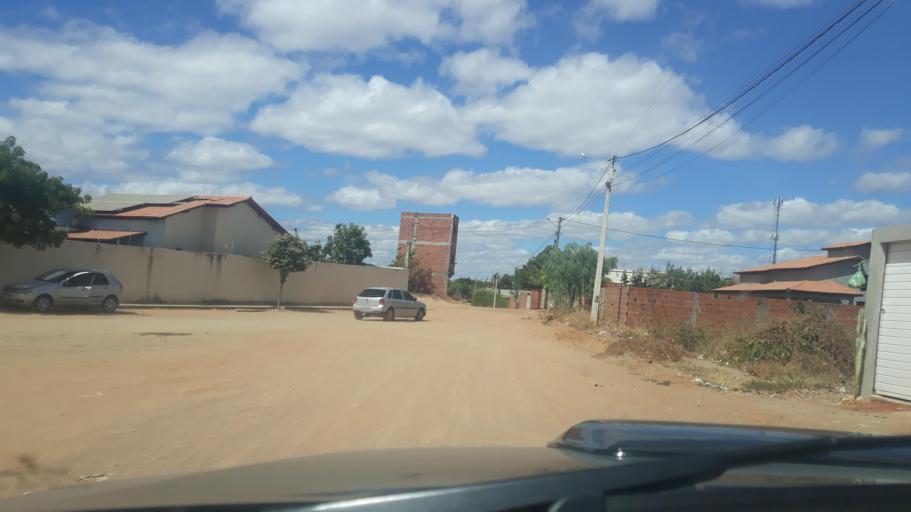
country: BR
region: Bahia
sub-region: Riacho De Santana
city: Riacho de Santana
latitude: -13.9060
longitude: -42.8494
